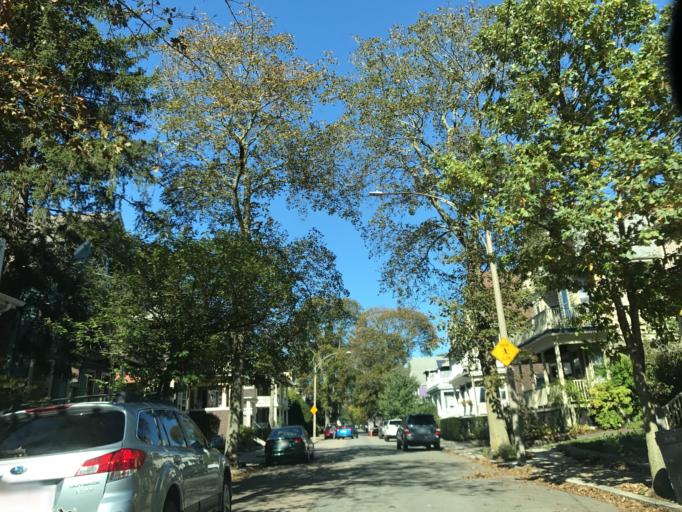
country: US
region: Massachusetts
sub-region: Suffolk County
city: Jamaica Plain
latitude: 42.3093
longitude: -71.1177
